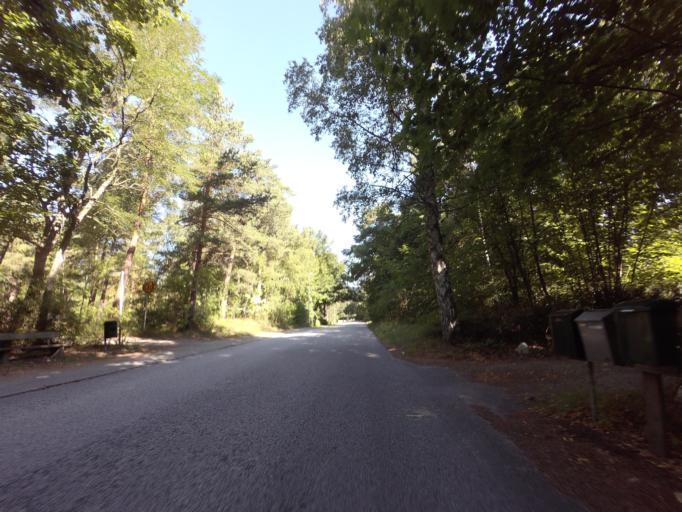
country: SE
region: Skane
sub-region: Ystads Kommun
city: Ystad
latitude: 55.4276
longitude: 13.8493
